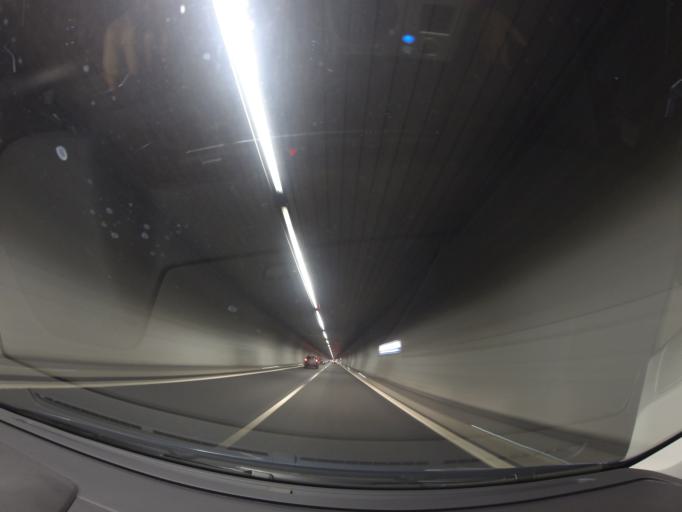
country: CH
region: Saint Gallen
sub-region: Wahlkreis See-Gaster
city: Amden
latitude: 47.1220
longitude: 9.1352
